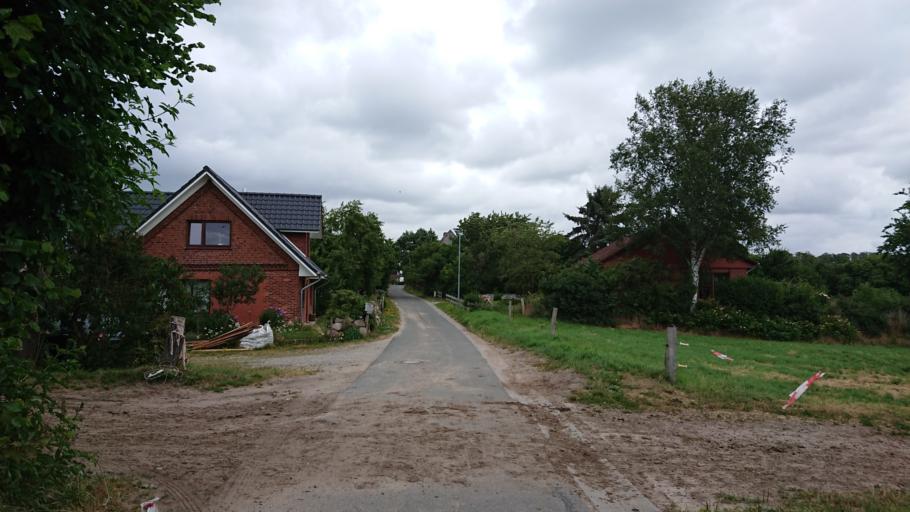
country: DE
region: Schleswig-Holstein
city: Gross Sarau
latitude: 53.7843
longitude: 10.7238
